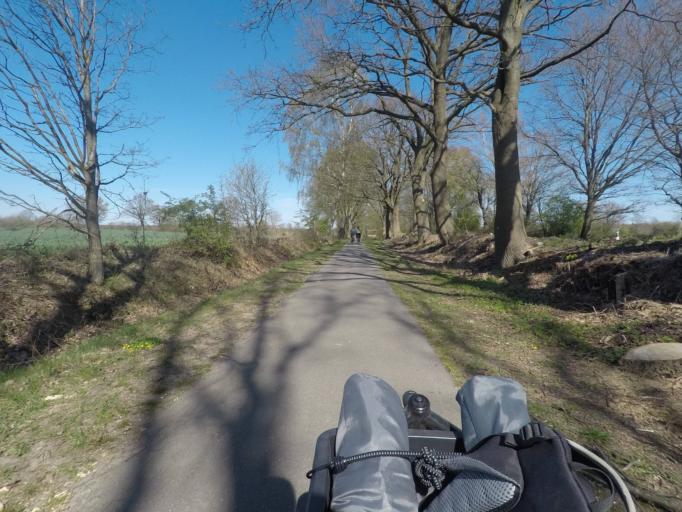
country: DE
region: Schleswig-Holstein
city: Braak
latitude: 53.5976
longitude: 10.2714
